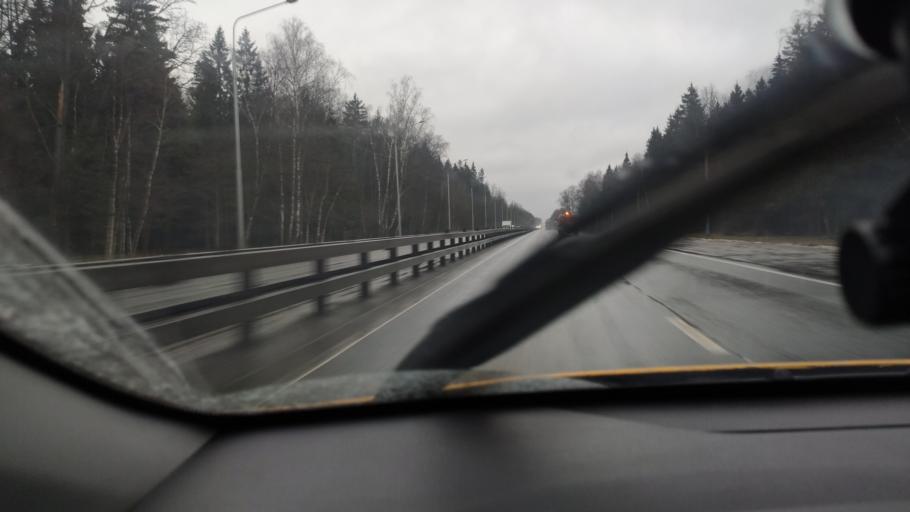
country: RU
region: Moskovskaya
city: Troitsk
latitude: 55.3446
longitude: 37.3193
